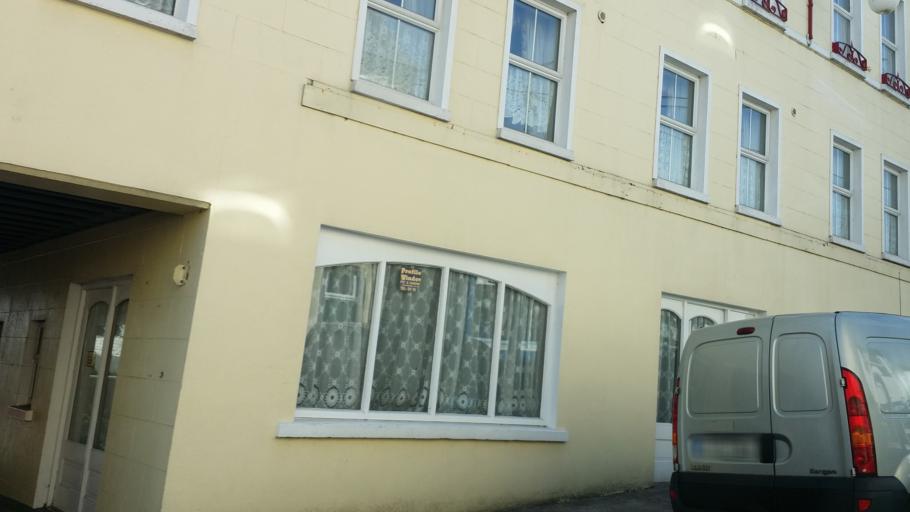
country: IE
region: Ulster
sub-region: County Donegal
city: Ballyshannon
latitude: 54.5021
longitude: -8.1910
